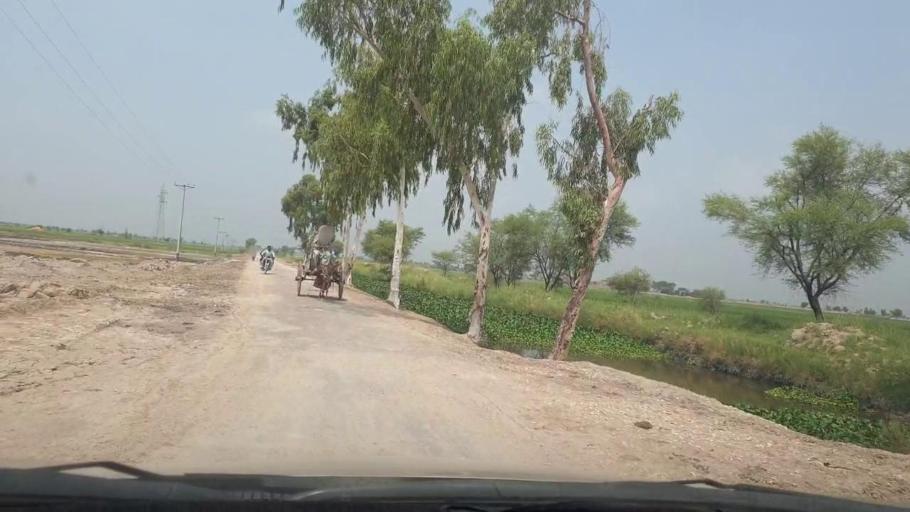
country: PK
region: Sindh
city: Naudero
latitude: 27.6871
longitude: 68.2644
